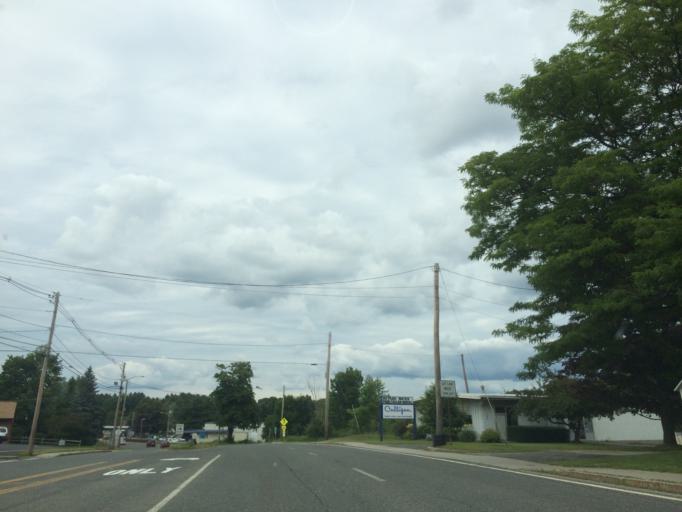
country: US
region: Massachusetts
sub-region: Berkshire County
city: Lenox
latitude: 42.3978
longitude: -73.2686
